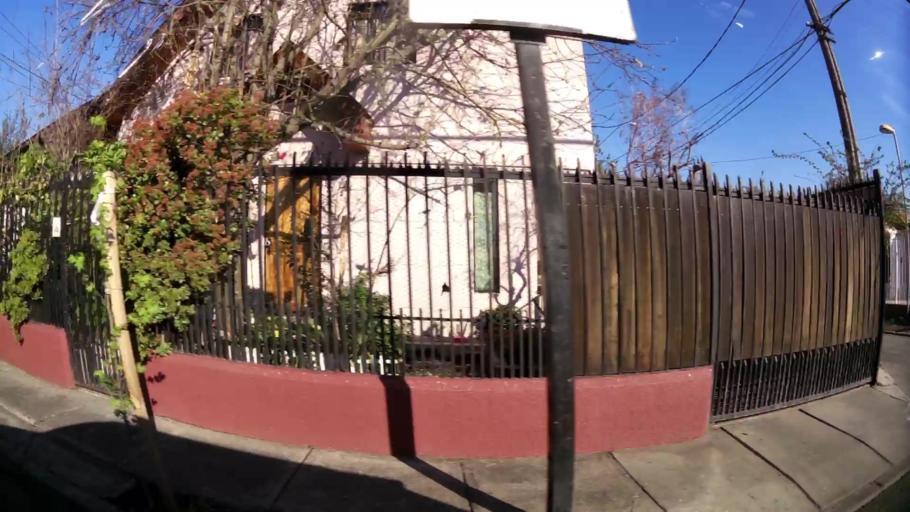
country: CL
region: Santiago Metropolitan
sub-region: Provincia de Santiago
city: Lo Prado
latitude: -33.4867
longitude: -70.7573
